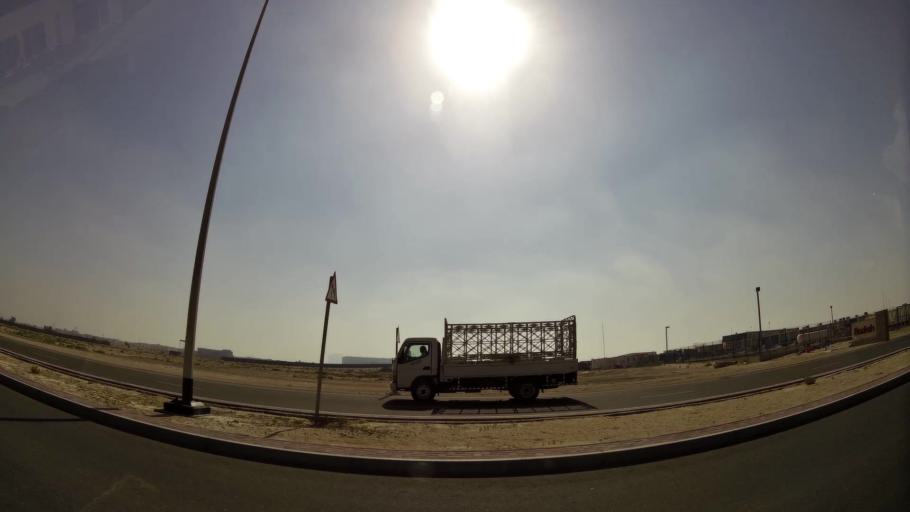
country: AE
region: Dubai
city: Dubai
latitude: 24.9515
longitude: 55.0512
